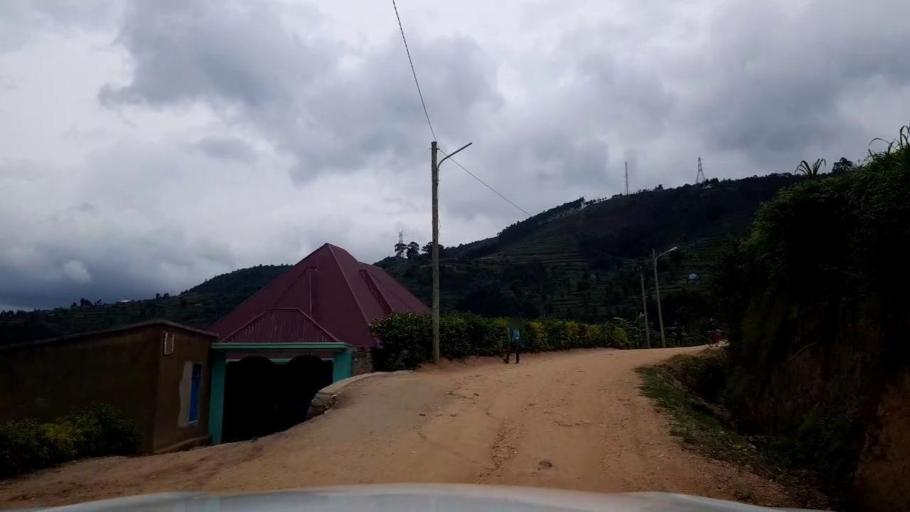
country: RW
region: Western Province
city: Kibuye
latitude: -1.9656
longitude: 29.3885
